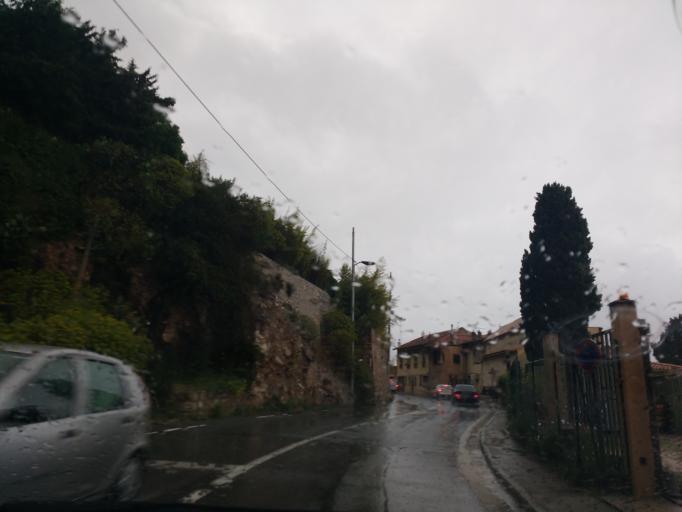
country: FR
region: Provence-Alpes-Cote d'Azur
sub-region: Departement des Alpes-Maritimes
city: Cap-d'Ail
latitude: 43.7238
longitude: 7.3863
